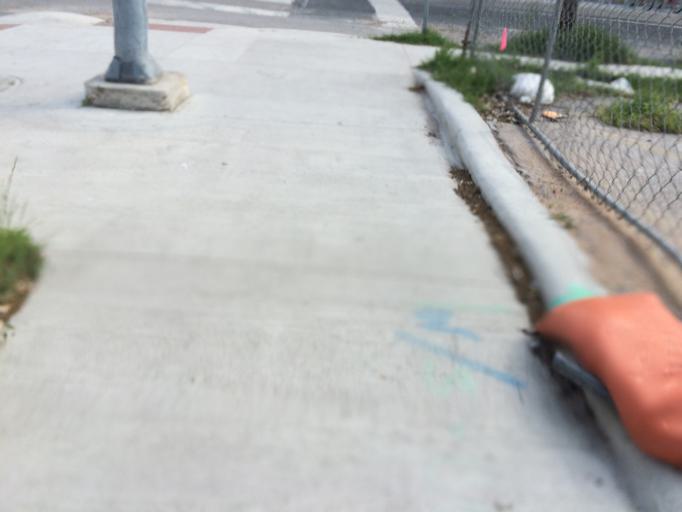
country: US
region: Texas
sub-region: Travis County
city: Austin
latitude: 30.2799
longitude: -97.7423
